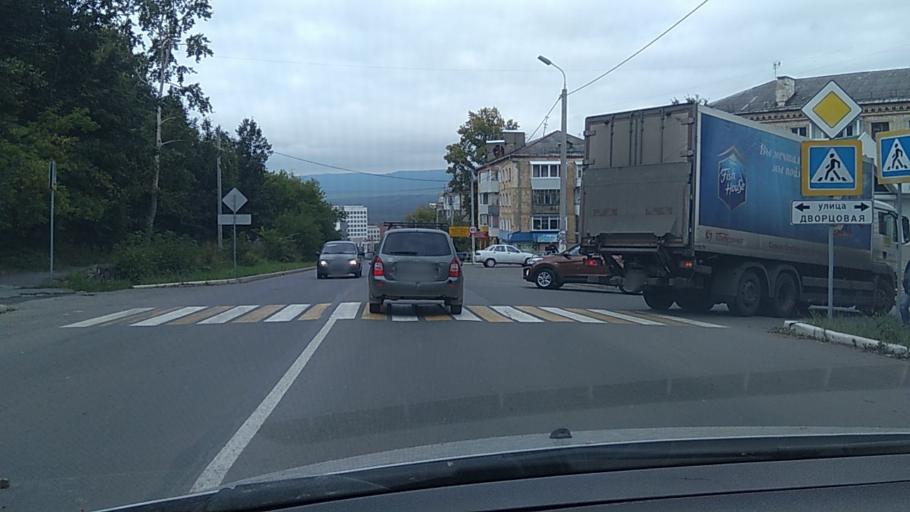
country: RU
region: Chelyabinsk
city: Zlatoust
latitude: 55.1146
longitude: 59.7202
